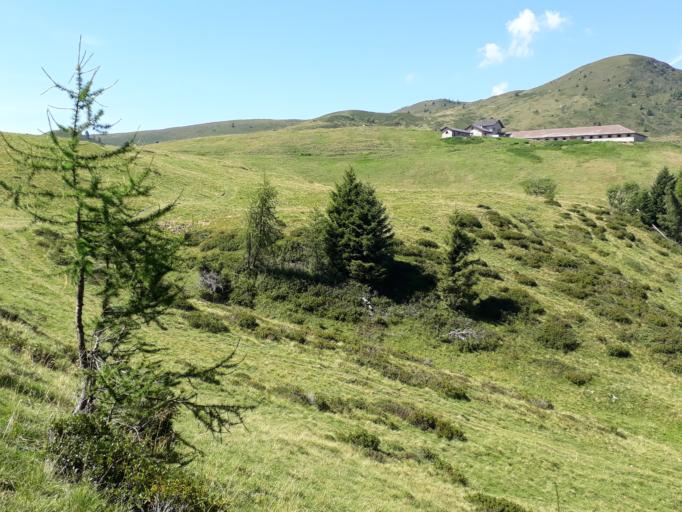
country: IT
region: Trentino-Alto Adige
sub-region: Provincia di Trento
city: Lodrone-Darzo
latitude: 45.8742
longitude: 10.5241
